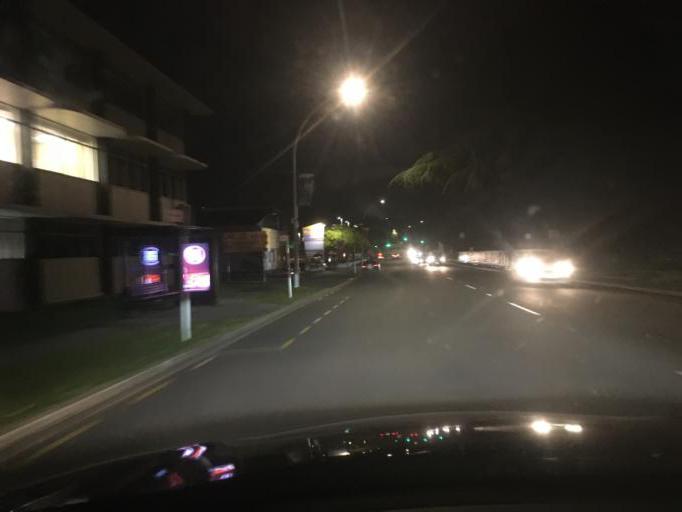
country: NZ
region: Waikato
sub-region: Hamilton City
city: Hamilton
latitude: -37.7861
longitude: 175.2752
